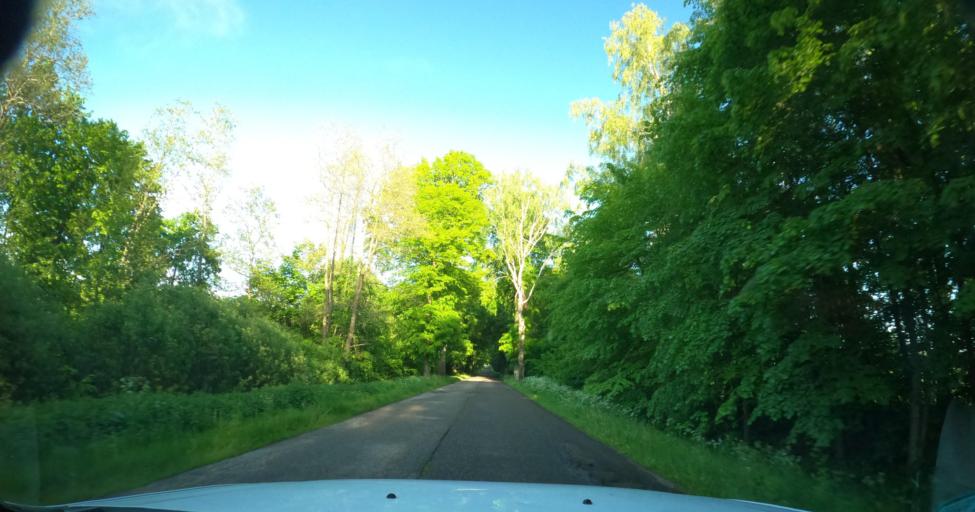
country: PL
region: Warmian-Masurian Voivodeship
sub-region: Powiat braniewski
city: Pieniezno
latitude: 54.2517
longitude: 20.0077
